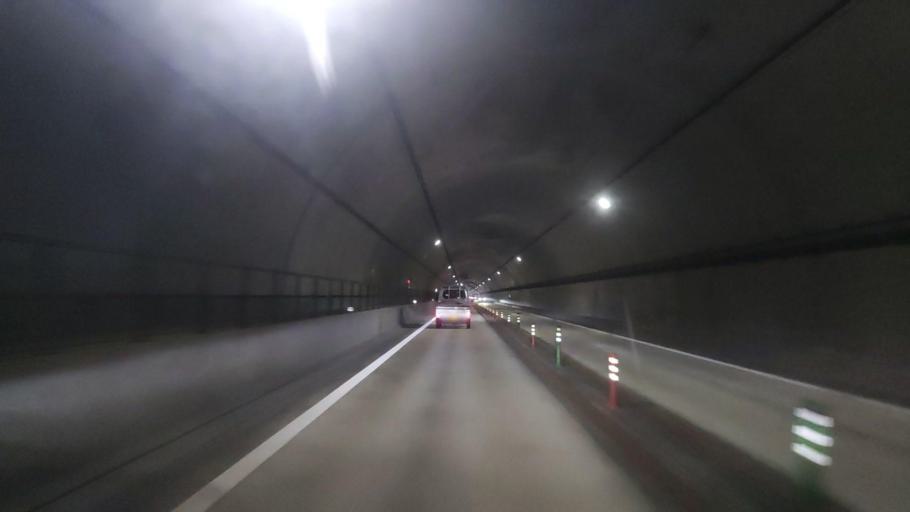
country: JP
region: Wakayama
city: Tanabe
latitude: 33.6260
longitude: 135.4169
